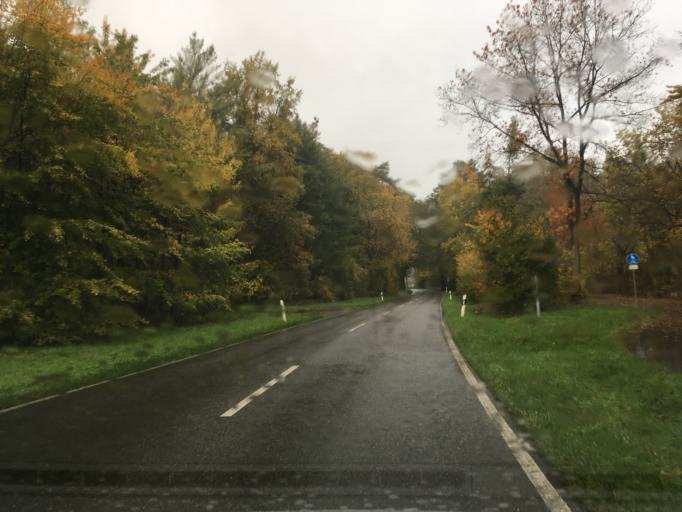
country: DE
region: North Rhine-Westphalia
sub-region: Regierungsbezirk Munster
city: Klein Reken
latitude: 51.8446
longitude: 7.0303
